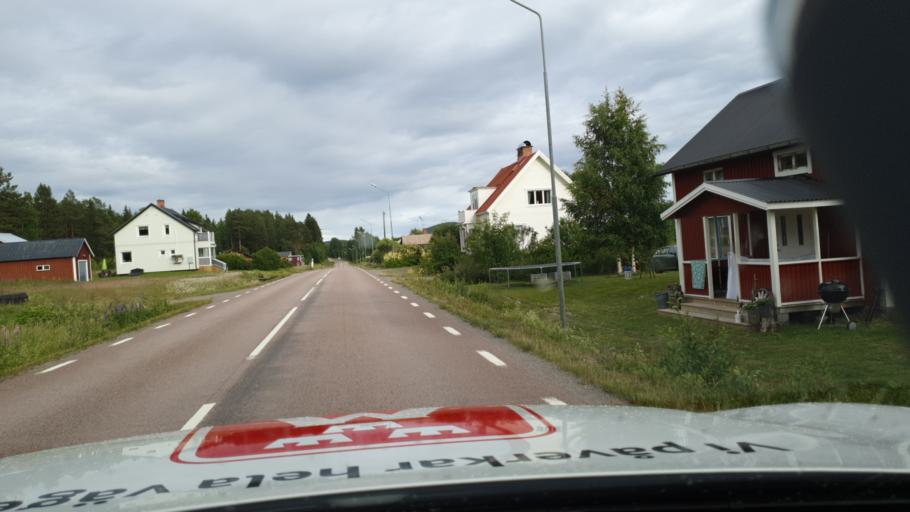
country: SE
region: Vaesternorrland
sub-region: Solleftea Kommun
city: As
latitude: 63.5954
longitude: 16.1683
